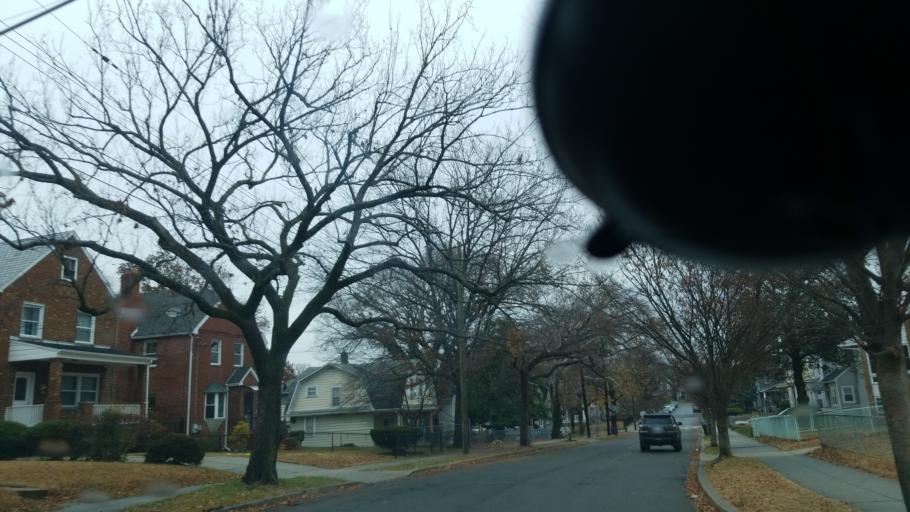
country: US
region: Maryland
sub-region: Prince George's County
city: Mount Rainier
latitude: 38.9234
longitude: -76.9821
